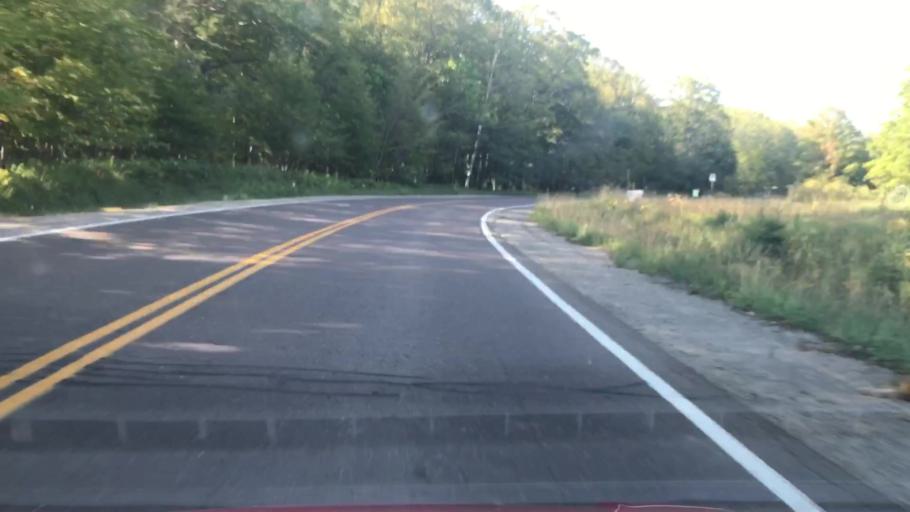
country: US
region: Michigan
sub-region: Chippewa County
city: Sault Ste. Marie
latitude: 46.2807
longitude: -84.0320
